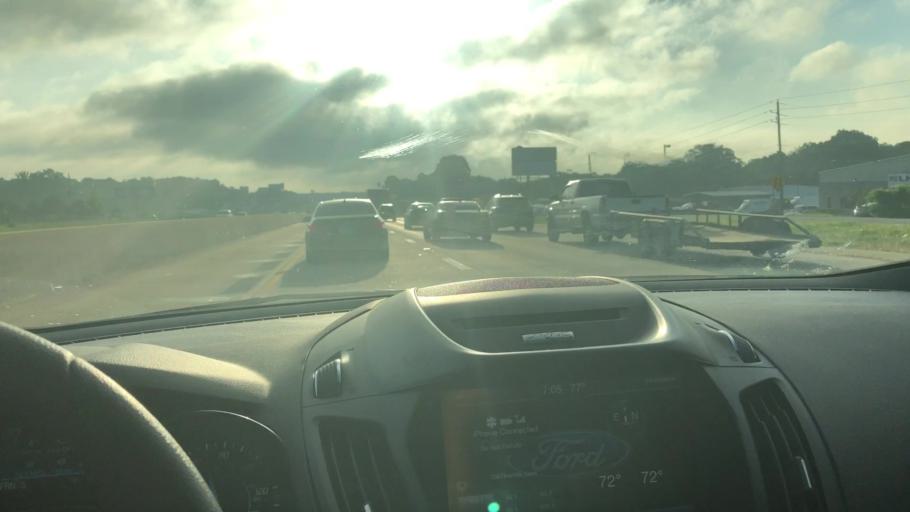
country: US
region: Arkansas
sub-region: Pulaski County
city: Alexander
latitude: 34.6357
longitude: -92.4575
